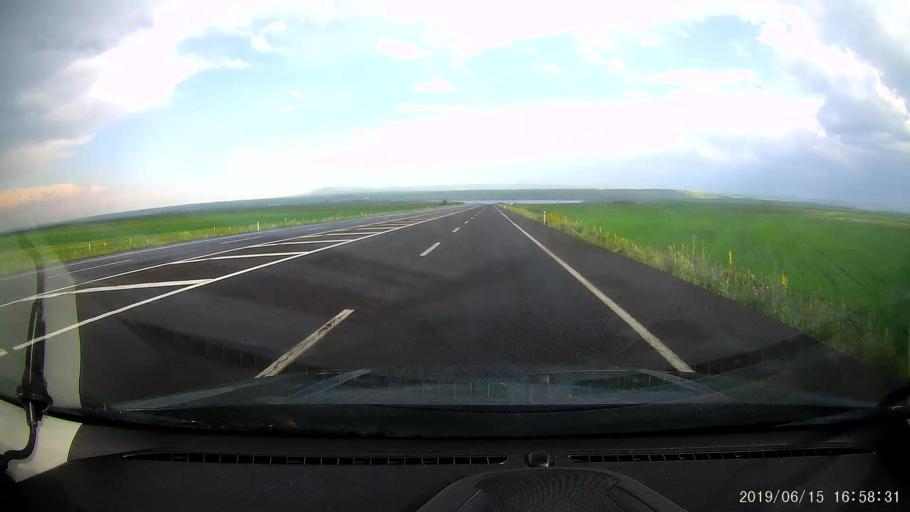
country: TR
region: Kars
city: Susuz
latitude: 40.7643
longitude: 43.1438
